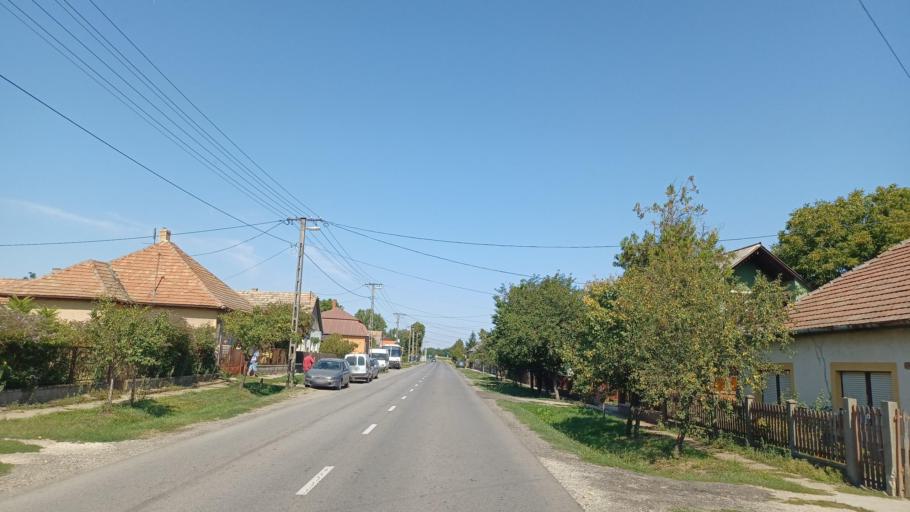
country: HU
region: Tolna
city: Nagydorog
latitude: 46.6319
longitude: 18.6548
